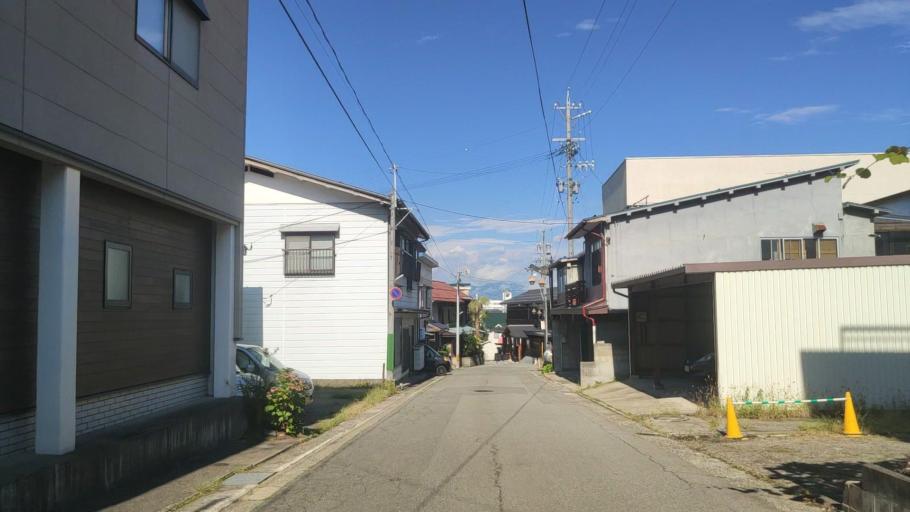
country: JP
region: Nagano
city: Nakano
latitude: 36.7402
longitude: 138.4168
